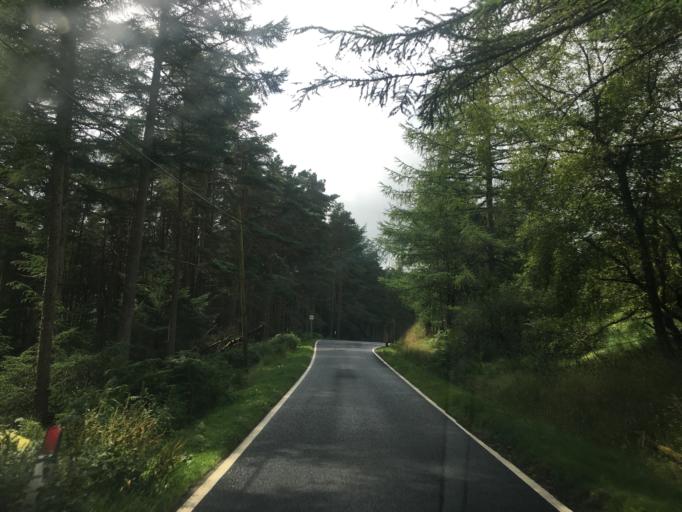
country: GB
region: Scotland
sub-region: Argyll and Bute
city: Port Bannatyne
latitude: 55.9997
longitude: -5.1079
